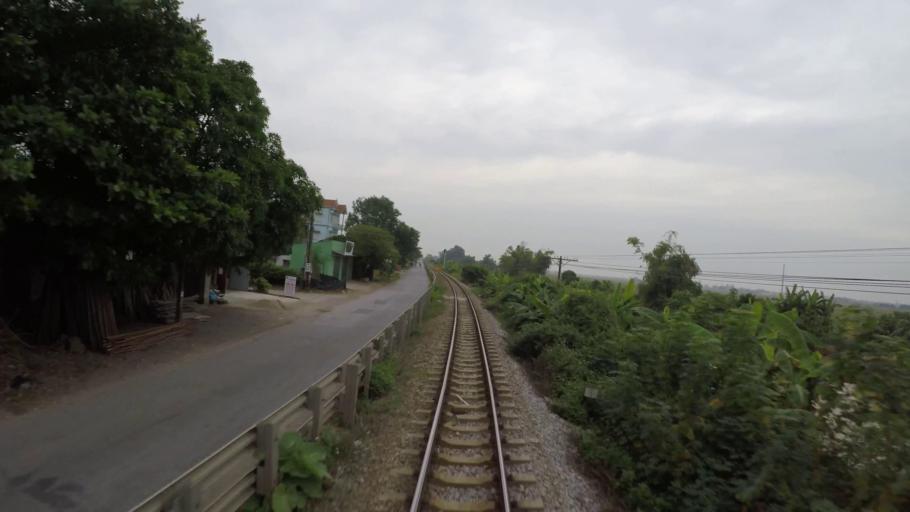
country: VN
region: Hung Yen
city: Ban Yen Nhan
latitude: 20.9692
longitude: 106.1037
